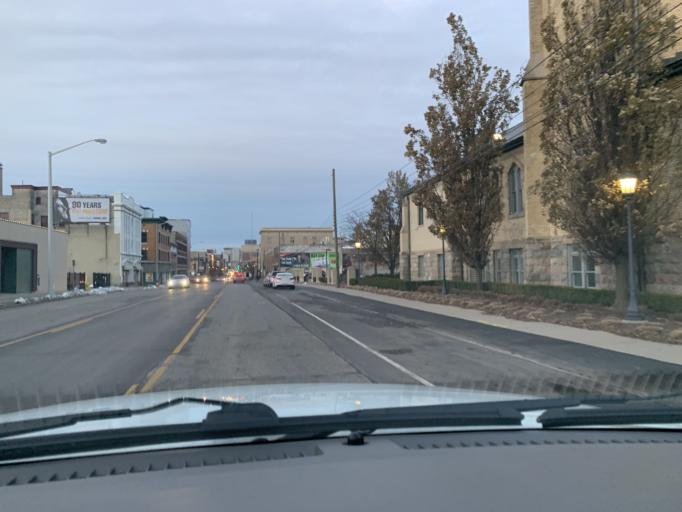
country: US
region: Michigan
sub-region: Kent County
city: Grand Rapids
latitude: 42.9579
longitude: -85.6677
